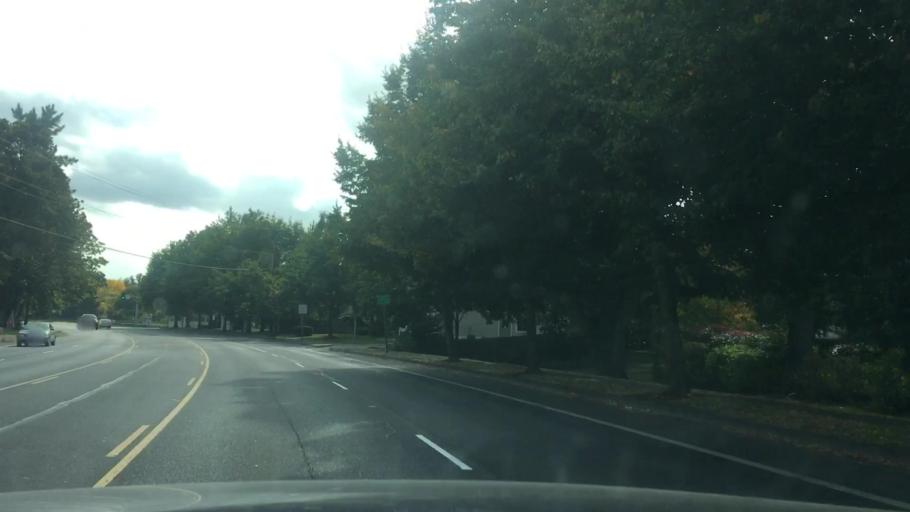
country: US
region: Oregon
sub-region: Lane County
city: Eugene
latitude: 44.0854
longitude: -123.1104
